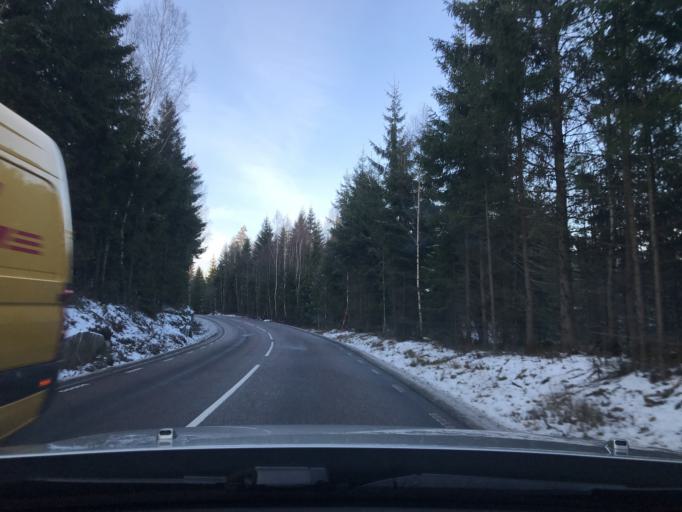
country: SE
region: Vaestra Goetaland
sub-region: Lerums Kommun
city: Stenkullen
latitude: 57.7222
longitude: 12.3479
